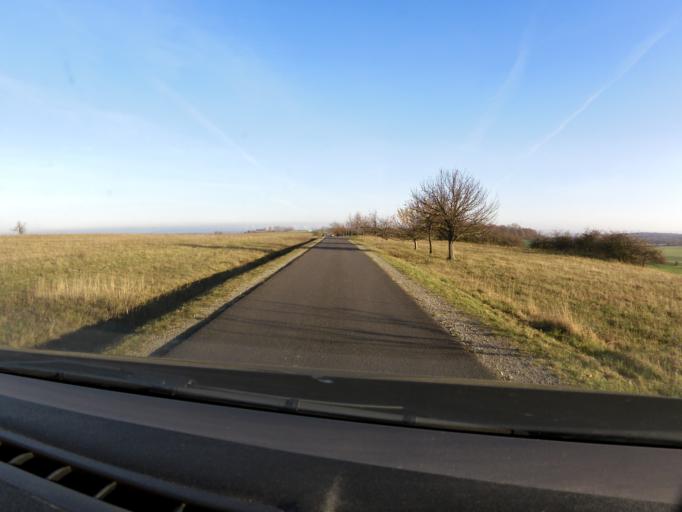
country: DE
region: Thuringia
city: Weberstedt
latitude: 51.0663
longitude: 10.4695
